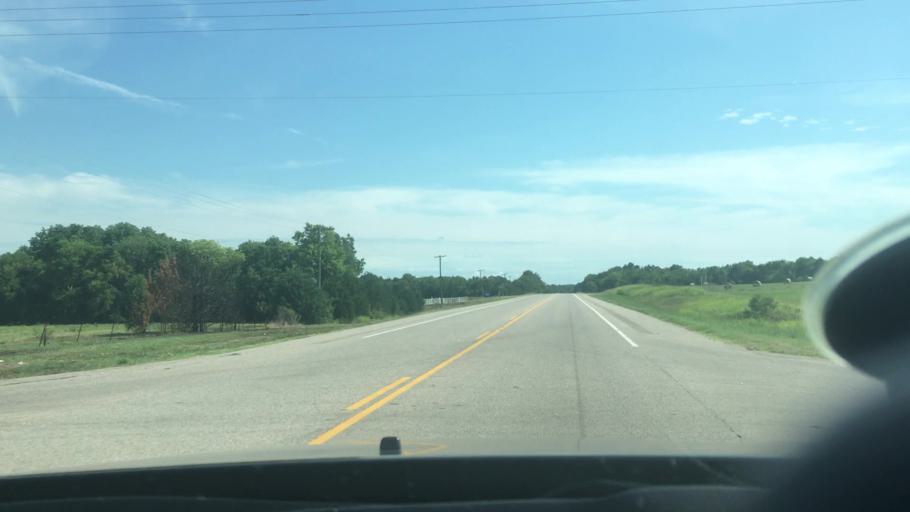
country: US
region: Oklahoma
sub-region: Seminole County
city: Konawa
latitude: 34.9710
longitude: -96.6790
